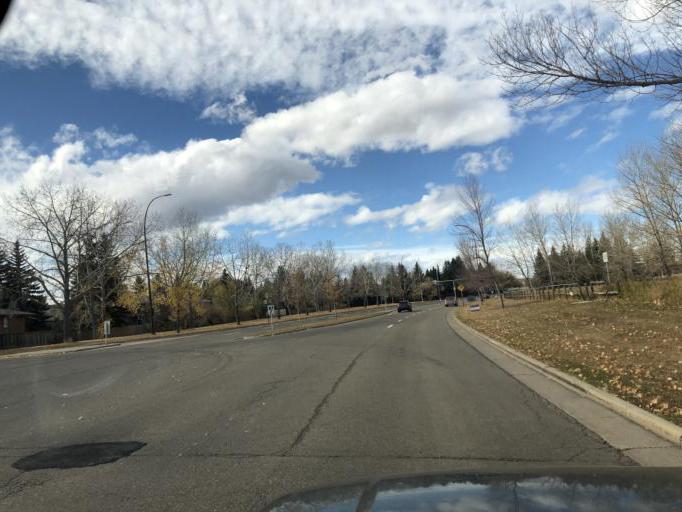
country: CA
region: Alberta
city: Calgary
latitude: 50.9760
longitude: -114.1331
